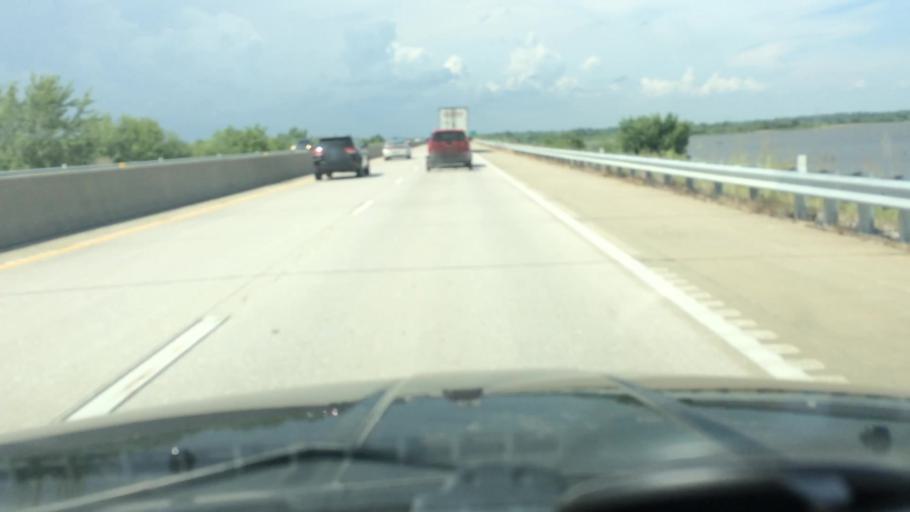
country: US
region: Missouri
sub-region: Henry County
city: Clinton
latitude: 38.3159
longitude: -93.7581
